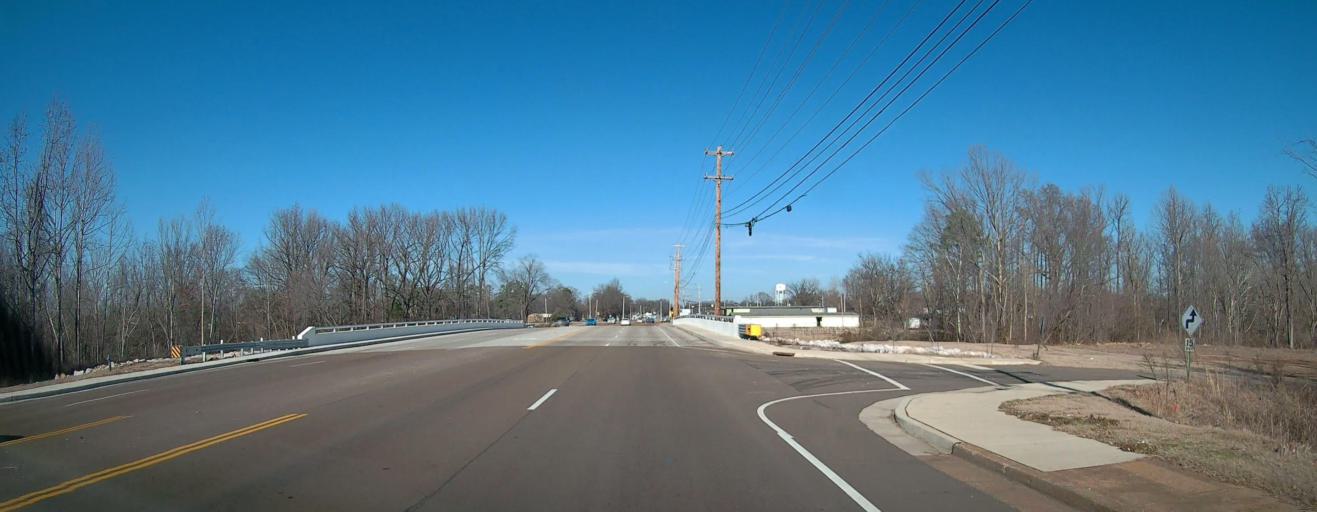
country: US
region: Tennessee
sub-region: Shelby County
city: Millington
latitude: 35.3321
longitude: -89.8981
